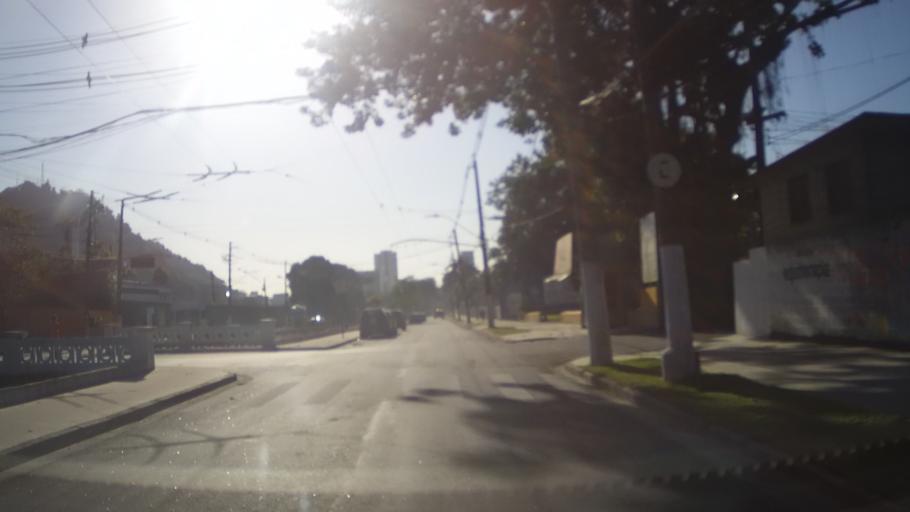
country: BR
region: Sao Paulo
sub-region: Santos
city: Santos
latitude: -23.9430
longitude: -46.3400
